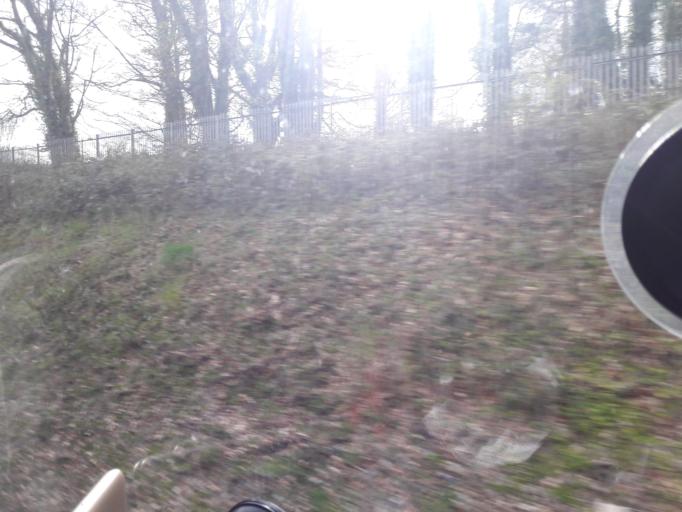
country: IE
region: Leinster
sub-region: An Iarmhi
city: An Muileann gCearr
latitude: 53.5263
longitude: -7.3478
